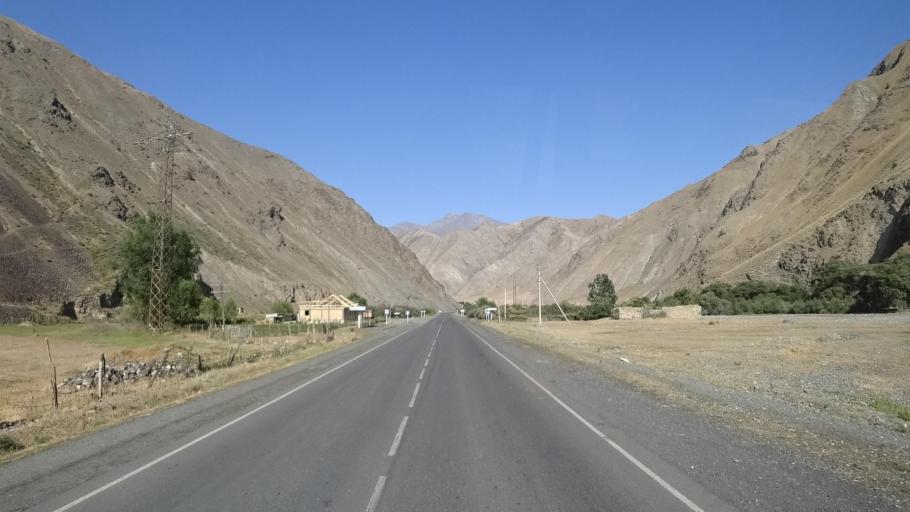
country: KG
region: Osh
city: Gul'cha
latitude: 40.0298
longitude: 73.5114
